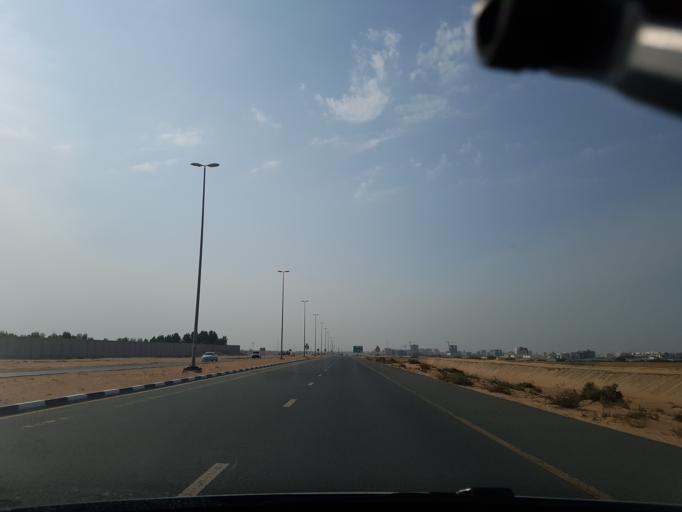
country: AE
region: Ajman
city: Ajman
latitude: 25.4126
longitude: 55.5609
